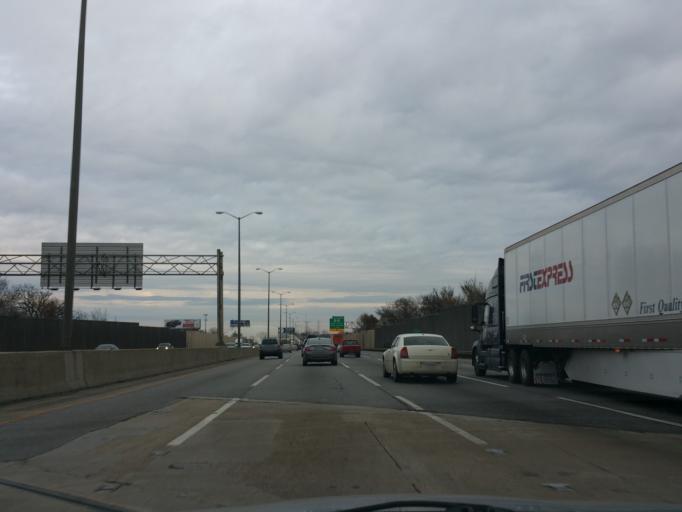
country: US
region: Illinois
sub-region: Cook County
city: Hickory Hills
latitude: 41.7332
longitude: -87.8183
